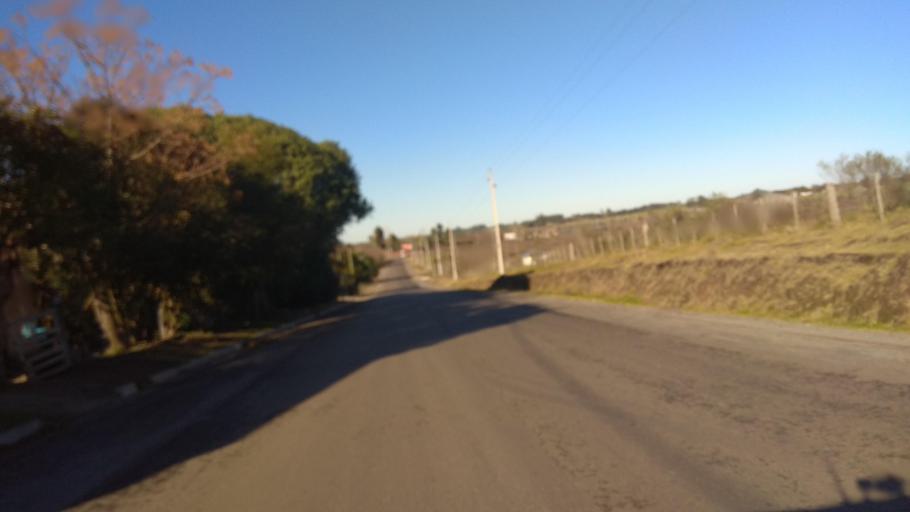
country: UY
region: Florida
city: Florida
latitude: -34.1004
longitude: -56.2416
